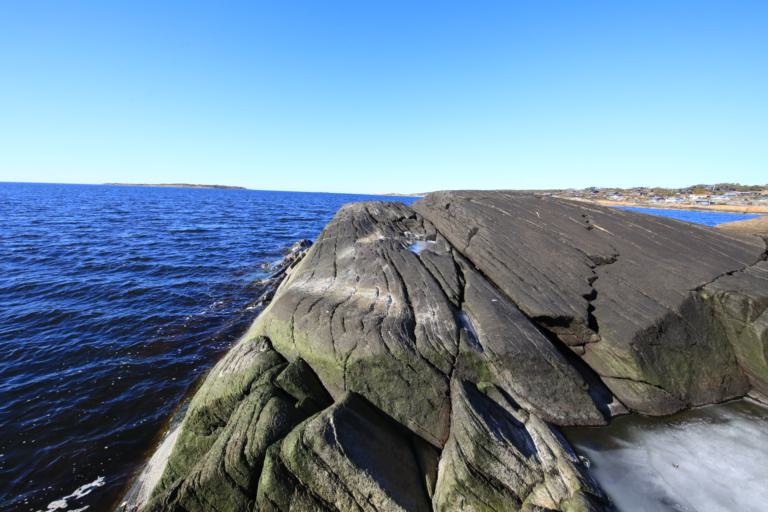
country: SE
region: Halland
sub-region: Kungsbacka Kommun
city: Frillesas
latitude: 57.2221
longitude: 12.1258
